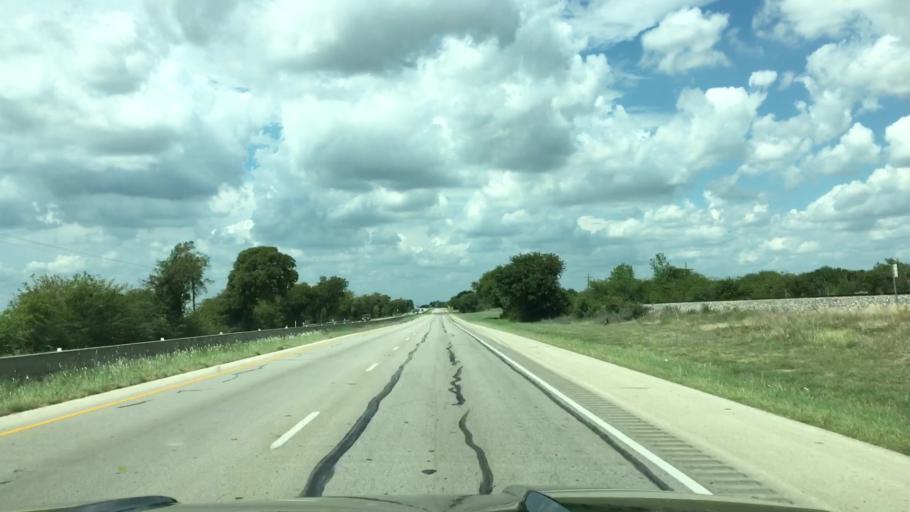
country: US
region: Texas
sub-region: Tarrant County
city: Eagle Mountain
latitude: 32.9129
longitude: -97.4062
